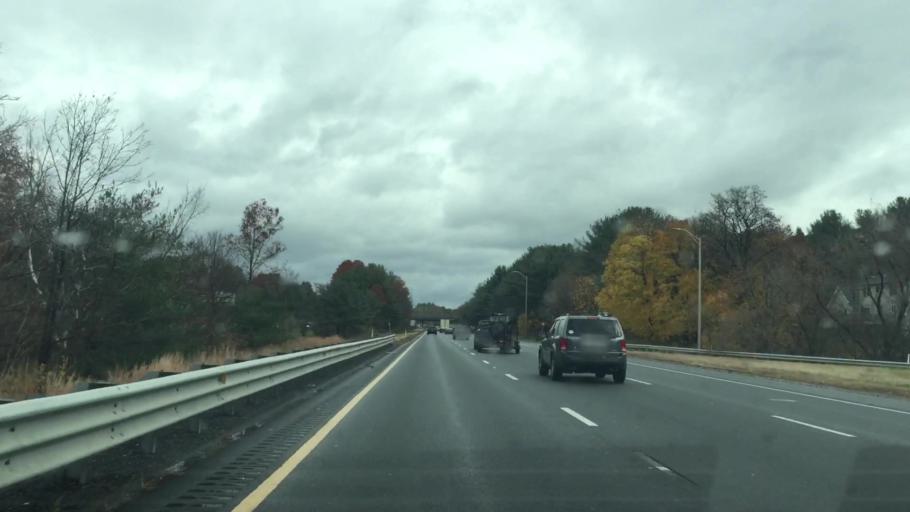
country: US
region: Massachusetts
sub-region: Essex County
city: Haverhill
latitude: 42.8017
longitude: -71.0900
